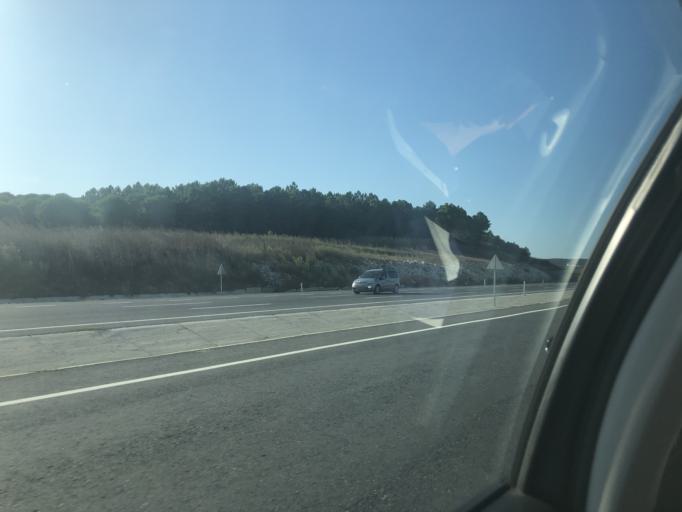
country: TR
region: Istanbul
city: Catalca
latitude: 41.2026
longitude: 28.4656
